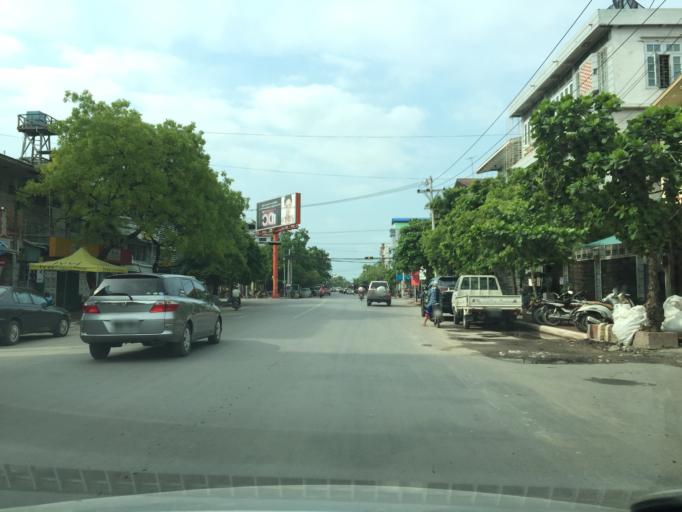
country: MM
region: Mandalay
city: Mandalay
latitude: 21.9701
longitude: 96.0804
